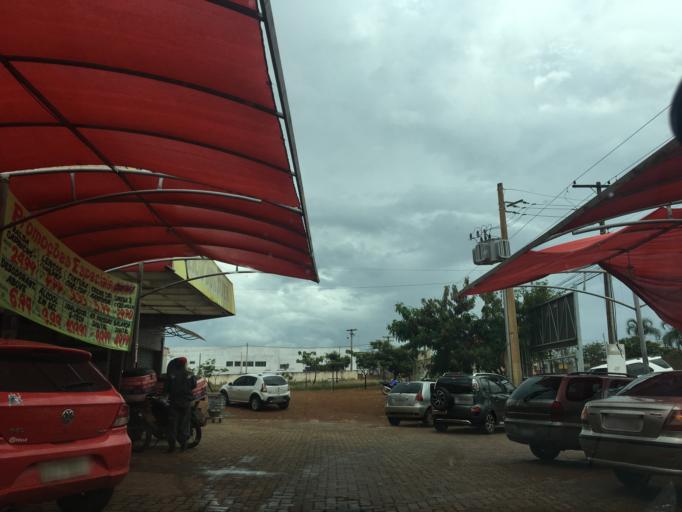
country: BR
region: Goias
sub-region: Luziania
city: Luziania
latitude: -16.2470
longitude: -47.9149
